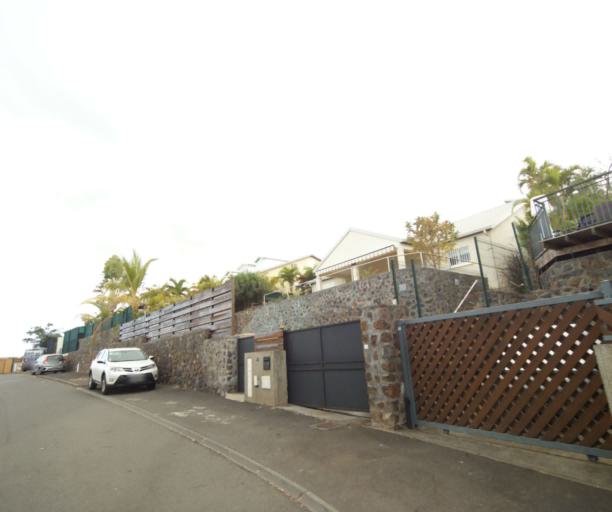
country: RE
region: Reunion
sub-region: Reunion
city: Saint-Paul
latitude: -21.0637
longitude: 55.2252
